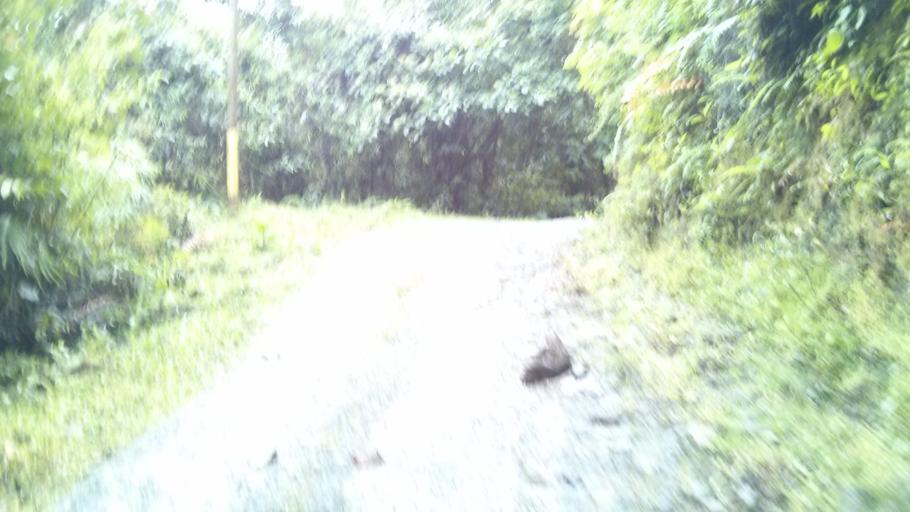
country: CR
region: San Jose
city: Ipis
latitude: 10.0310
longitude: -83.9313
